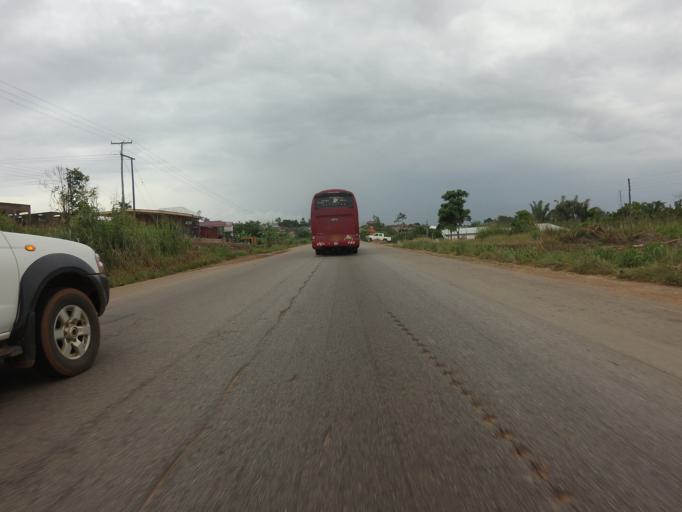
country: GH
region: Ashanti
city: Konongo
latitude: 6.6170
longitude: -1.1775
